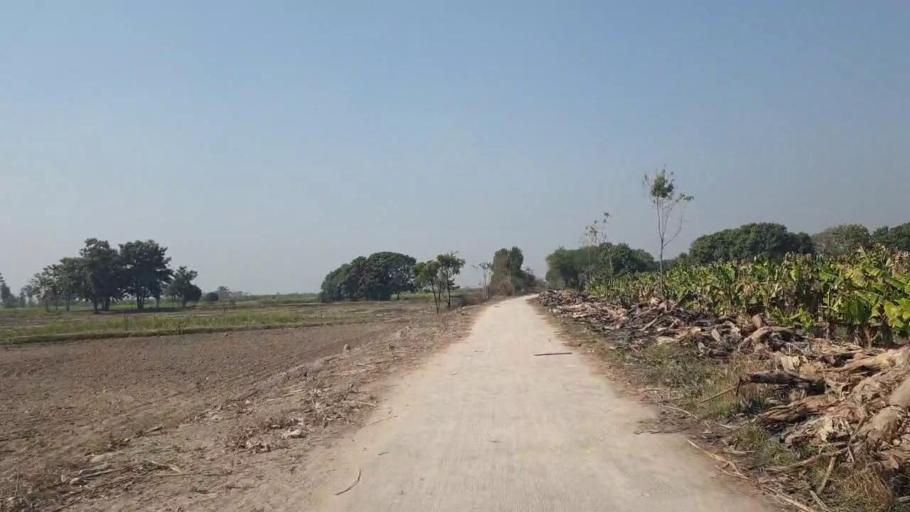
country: PK
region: Sindh
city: Chambar
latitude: 25.3485
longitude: 68.8509
